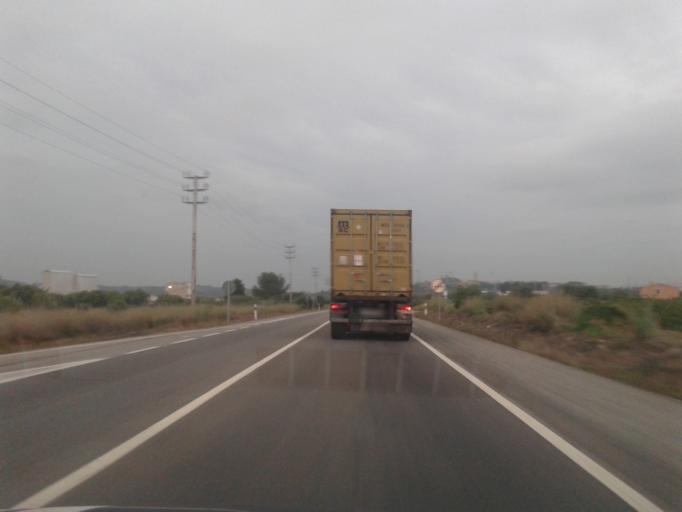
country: ES
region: Catalonia
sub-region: Provincia de Barcelona
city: Castellet
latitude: 41.2810
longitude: 1.6136
